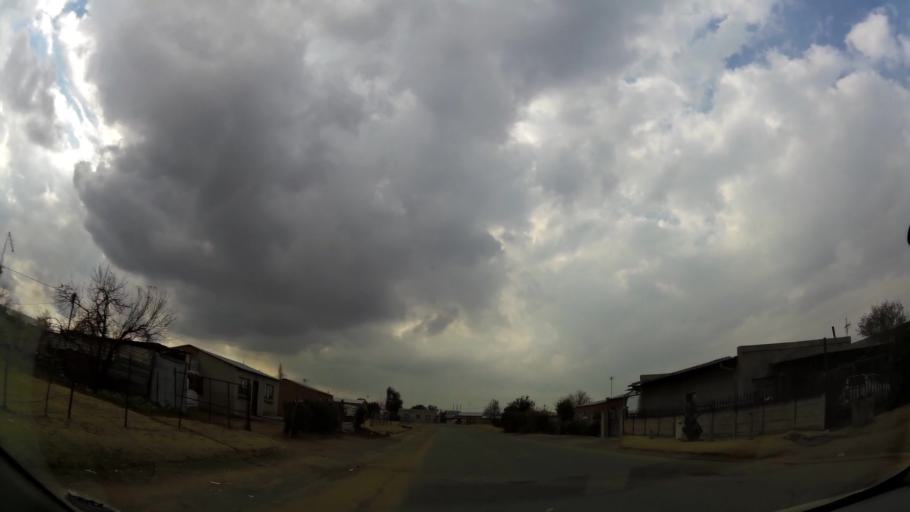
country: ZA
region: Orange Free State
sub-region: Fezile Dabi District Municipality
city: Sasolburg
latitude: -26.8488
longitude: 27.8781
